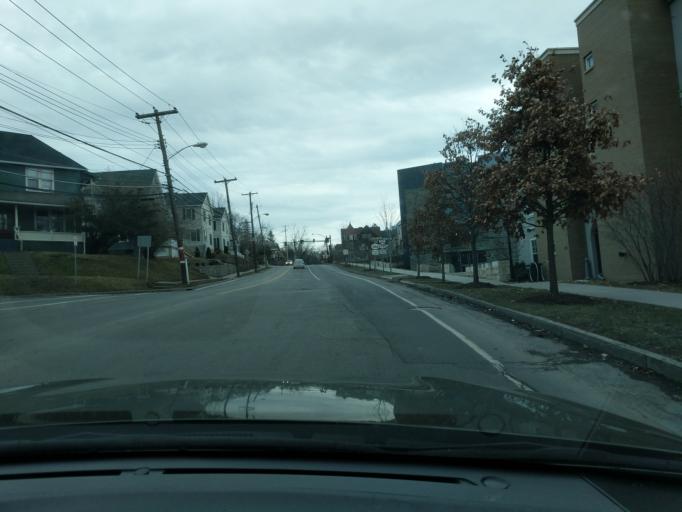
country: US
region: New York
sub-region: Tompkins County
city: East Ithaca
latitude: 42.4381
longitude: -76.4876
